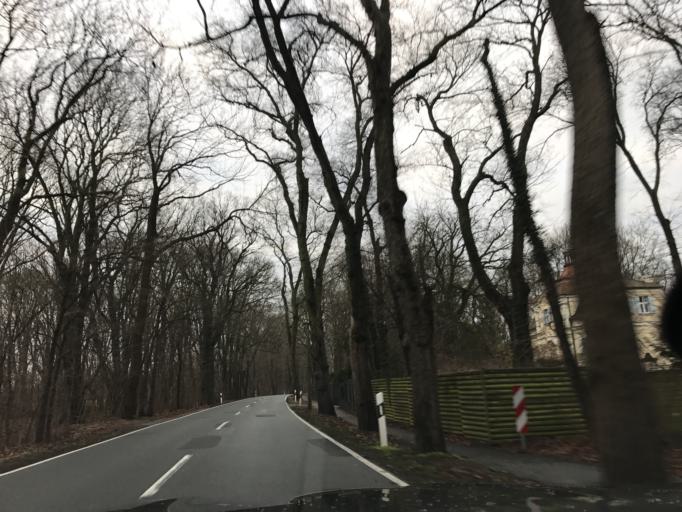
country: DE
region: Brandenburg
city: Werder
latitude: 52.3808
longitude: 12.9564
